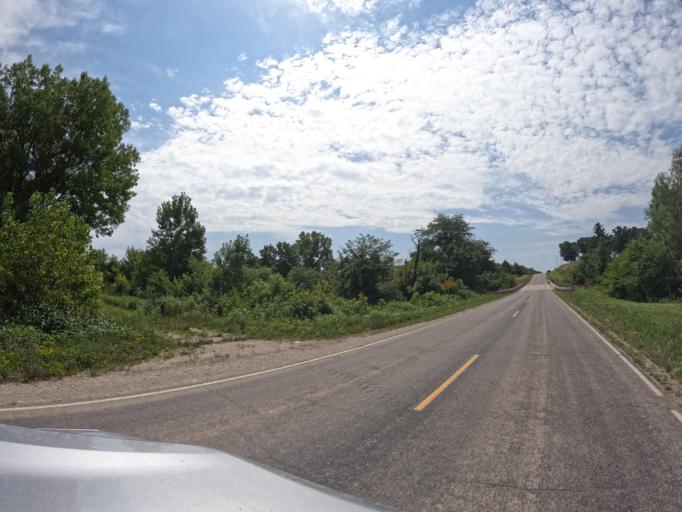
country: US
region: Iowa
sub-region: Appanoose County
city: Centerville
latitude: 40.7966
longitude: -92.9447
